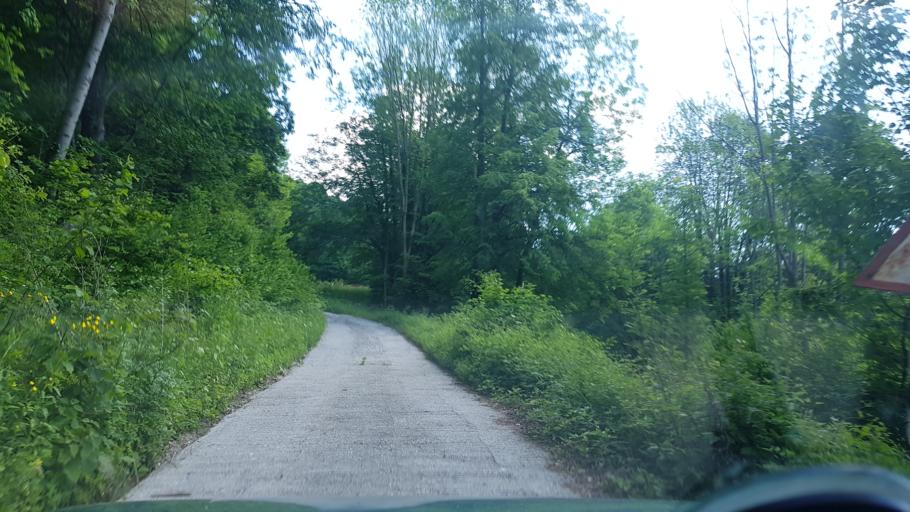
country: IT
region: Friuli Venezia Giulia
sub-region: Provincia di Udine
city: Torreano
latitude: 46.1780
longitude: 13.4302
